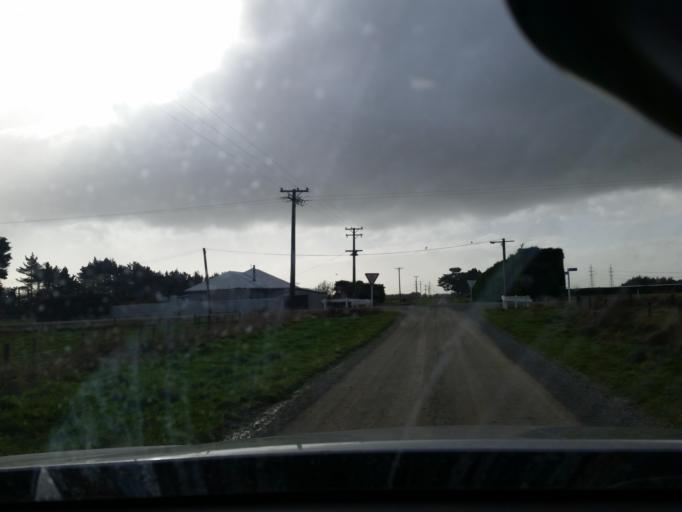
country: NZ
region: Southland
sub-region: Invercargill City
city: Invercargill
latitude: -46.3230
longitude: 168.3661
